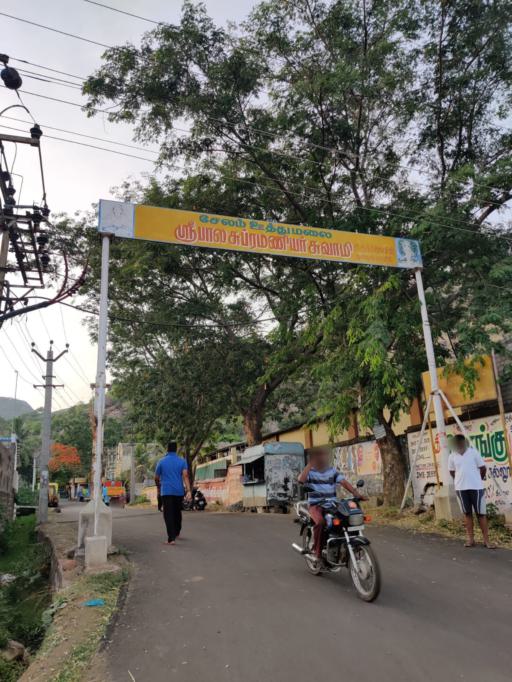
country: IN
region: Tamil Nadu
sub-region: Salem
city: Salem
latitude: 11.6219
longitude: 78.1465
